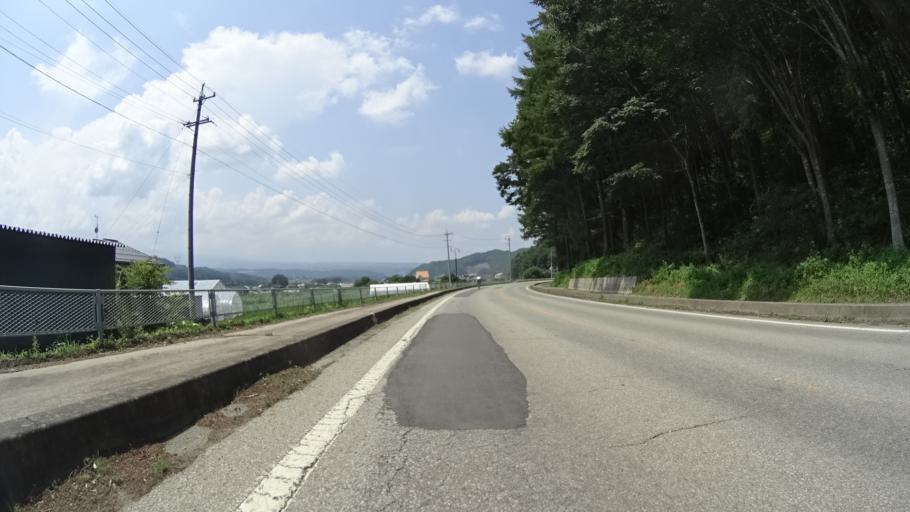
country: JP
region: Nagano
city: Saku
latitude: 36.1479
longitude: 138.5133
